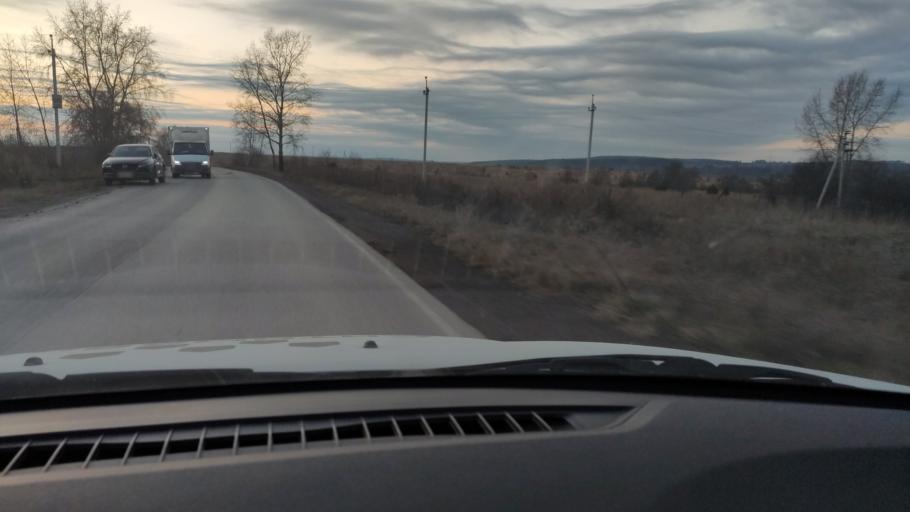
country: RU
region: Perm
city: Lobanovo
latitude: 57.8074
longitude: 56.3498
